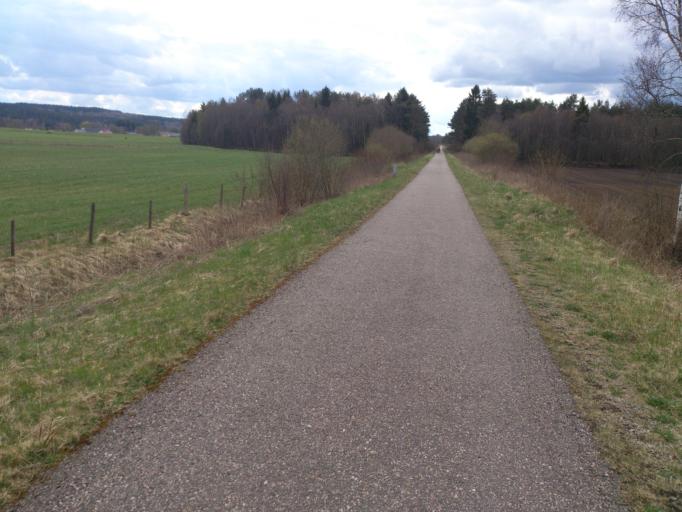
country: SE
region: Vaestra Goetaland
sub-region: Ulricehamns Kommun
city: Ulricehamn
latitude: 57.9654
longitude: 13.5153
